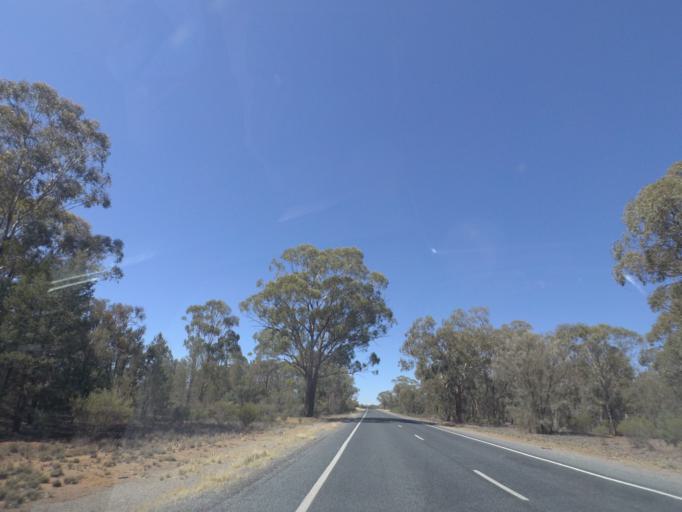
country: AU
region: New South Wales
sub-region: Narrandera
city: Narrandera
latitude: -34.4432
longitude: 146.8406
